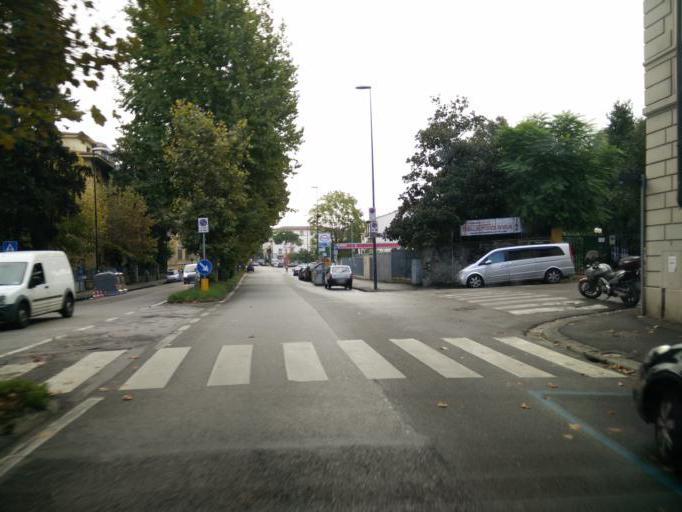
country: IT
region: Tuscany
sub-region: Province of Florence
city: Florence
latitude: 43.7699
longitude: 11.2343
